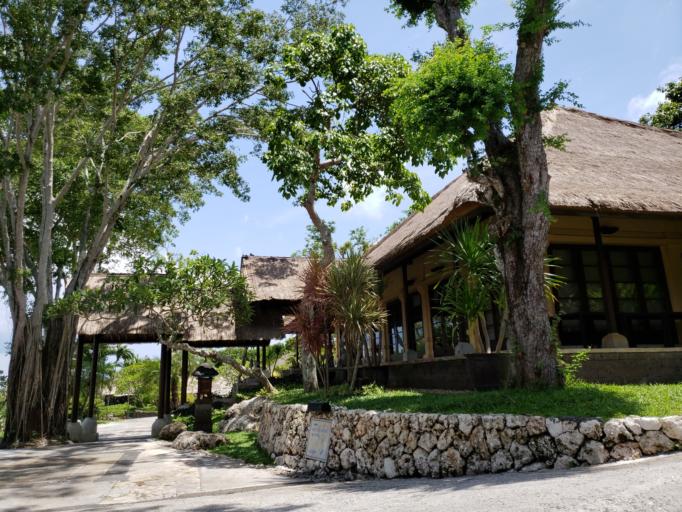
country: ID
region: Bali
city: Jimbaran
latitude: -8.7829
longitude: 115.1582
